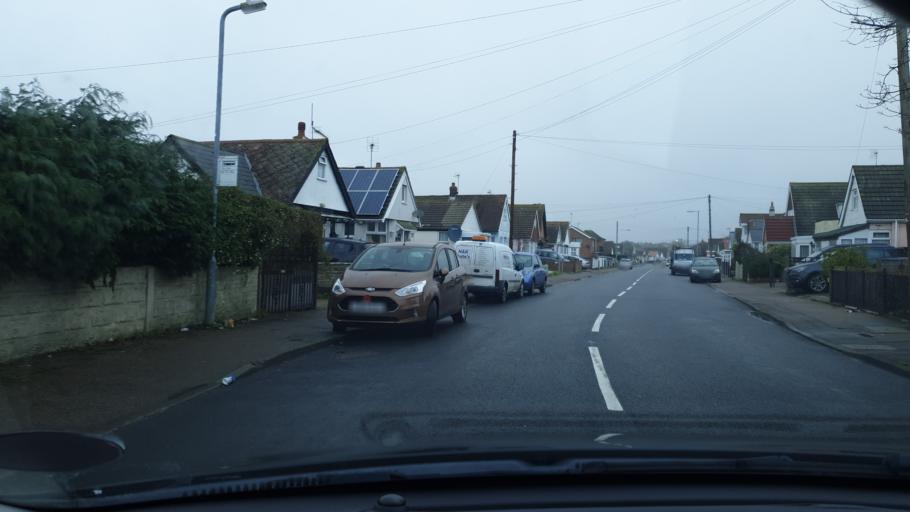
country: GB
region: England
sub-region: Essex
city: Clacton-on-Sea
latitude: 51.7775
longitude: 1.1216
